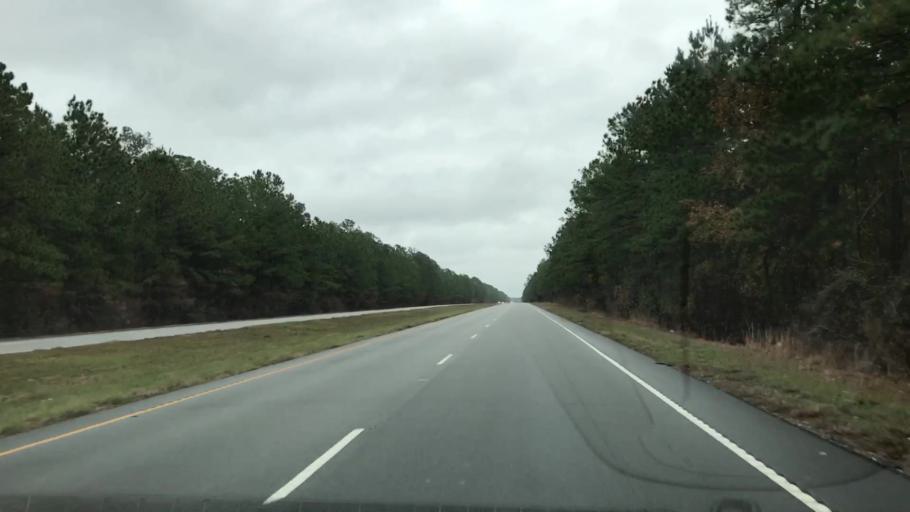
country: US
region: South Carolina
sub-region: Charleston County
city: Awendaw
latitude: 33.1513
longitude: -79.4324
